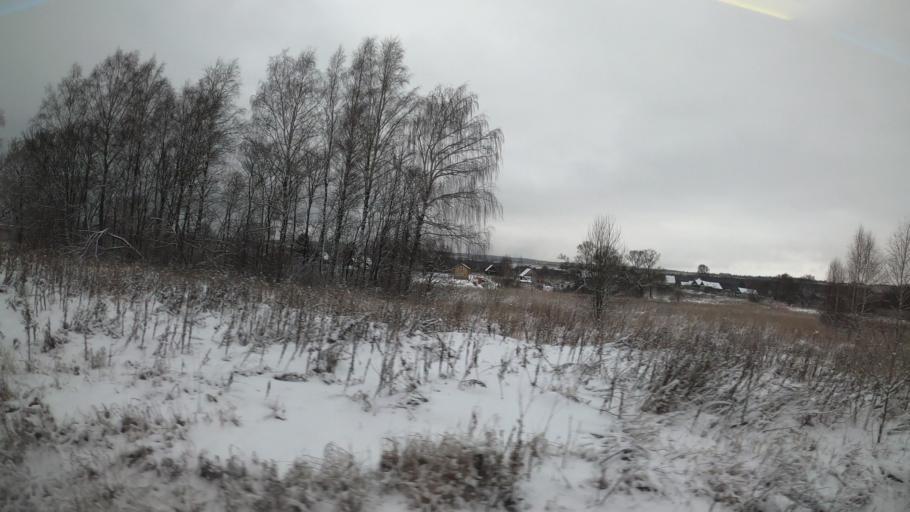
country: RU
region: Jaroslavl
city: Pereslavl'-Zalesskiy
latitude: 56.6826
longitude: 38.9195
